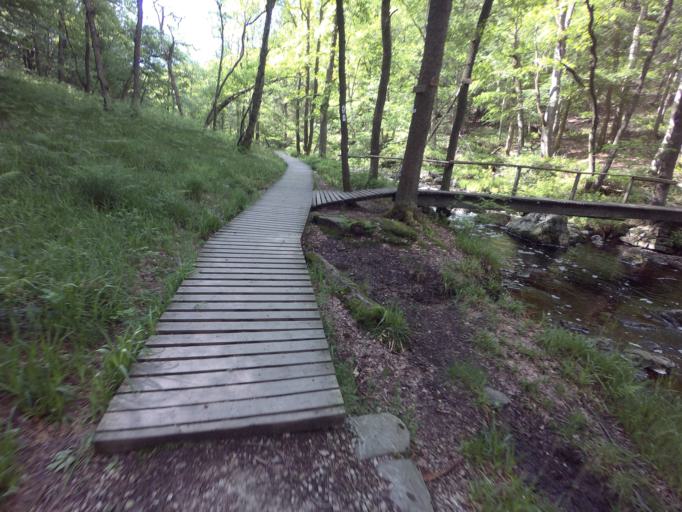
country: BE
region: Wallonia
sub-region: Province de Liege
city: Jalhay
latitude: 50.4987
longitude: 5.9803
